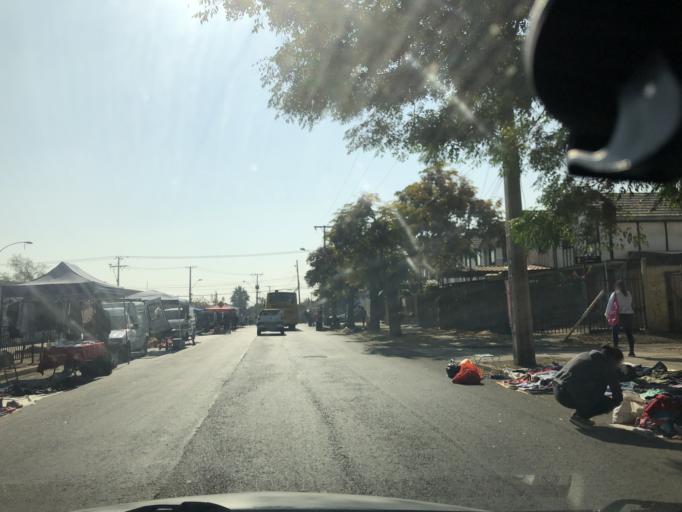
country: CL
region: Santiago Metropolitan
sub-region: Provincia de Cordillera
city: Puente Alto
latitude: -33.6015
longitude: -70.5579
